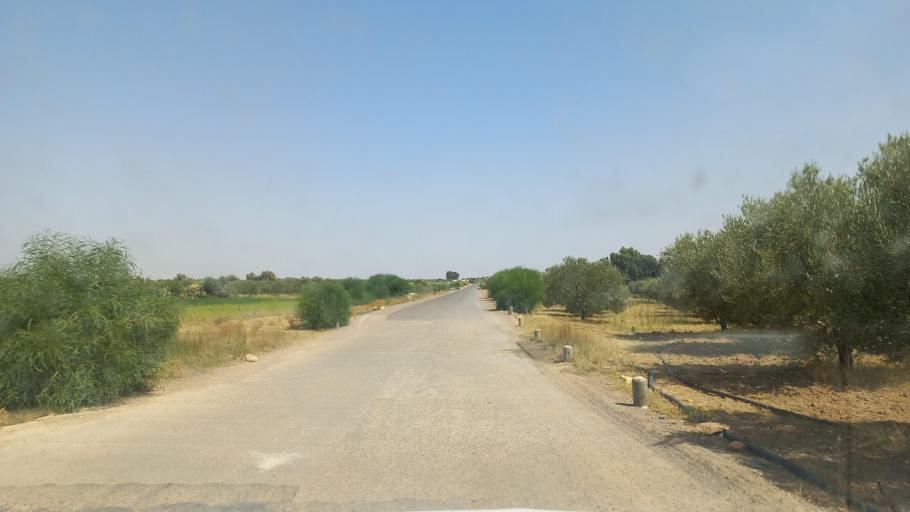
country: TN
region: Al Qasrayn
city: Kasserine
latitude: 35.2358
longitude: 9.0369
